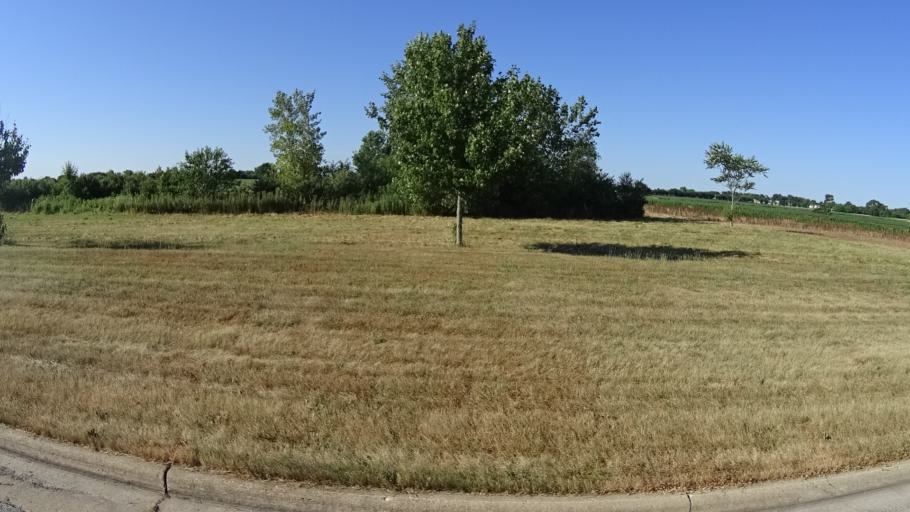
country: US
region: Ohio
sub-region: Erie County
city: Sandusky
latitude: 41.4108
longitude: -82.7607
